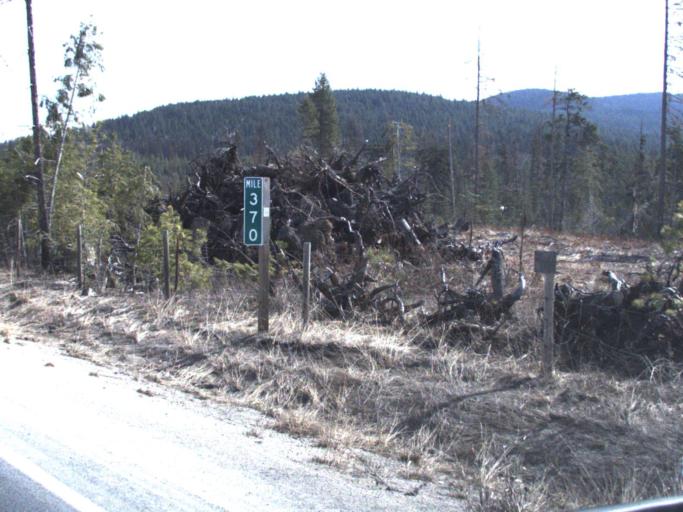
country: US
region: Washington
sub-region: Stevens County
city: Chewelah
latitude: 48.5194
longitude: -117.6477
